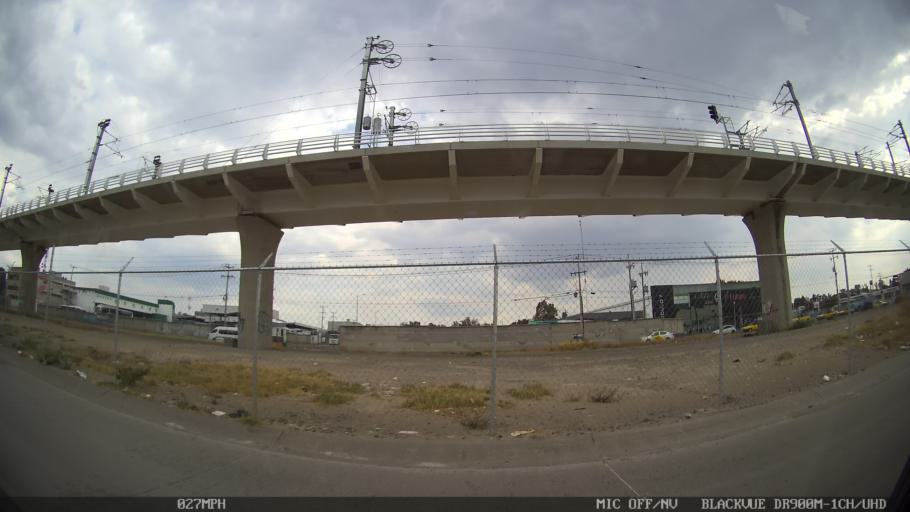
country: MX
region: Jalisco
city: Tlaquepaque
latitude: 20.6228
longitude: -103.2833
